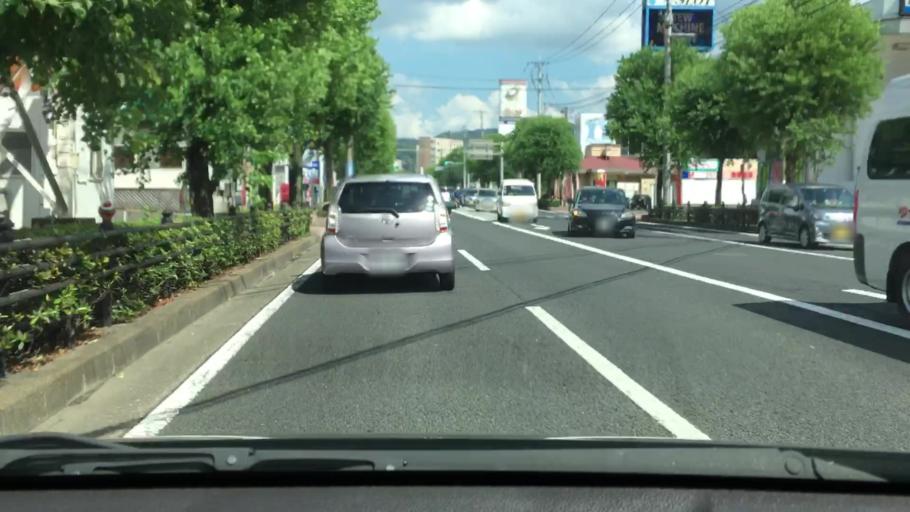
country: JP
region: Nagasaki
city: Sasebo
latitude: 33.2082
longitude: 129.7167
